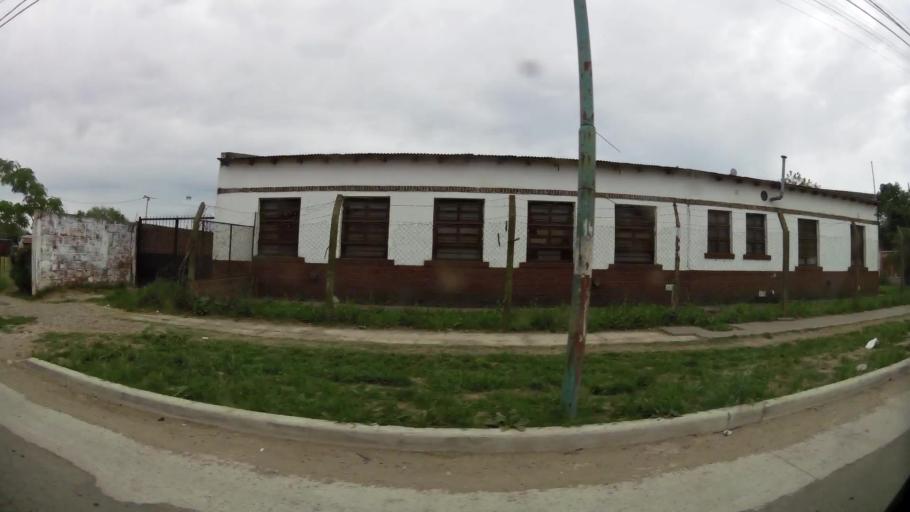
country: AR
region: Buenos Aires
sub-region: Partido de Zarate
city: Zarate
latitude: -34.1129
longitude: -59.0274
